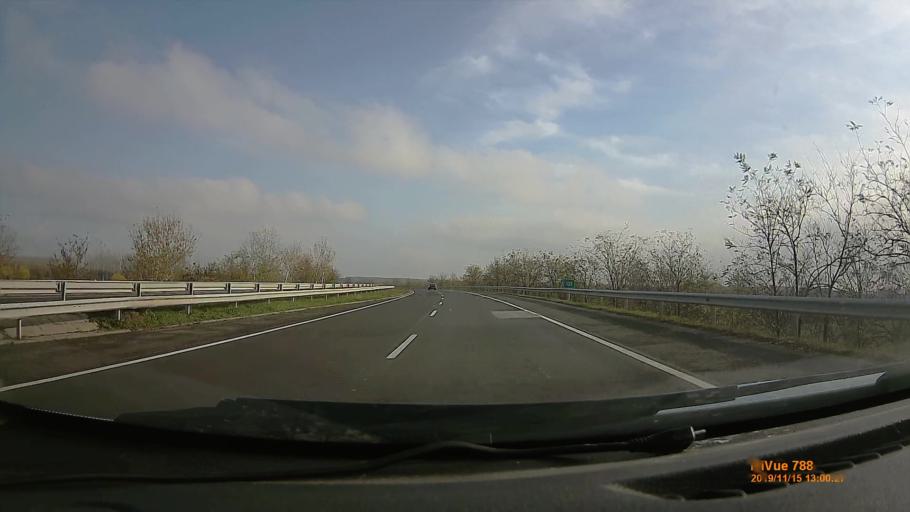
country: HU
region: Bekes
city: Gyula
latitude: 46.6590
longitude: 21.2073
